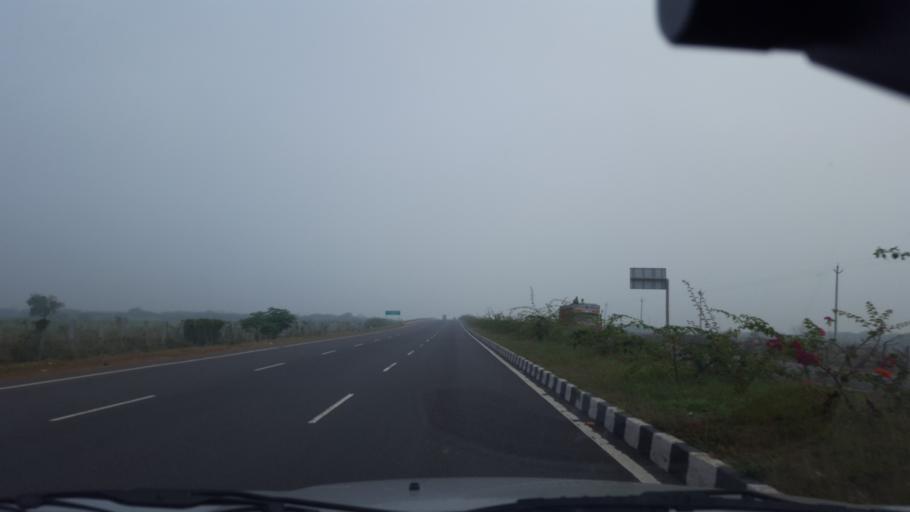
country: IN
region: Andhra Pradesh
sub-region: Prakasam
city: Ongole
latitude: 15.5005
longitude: 80.0698
